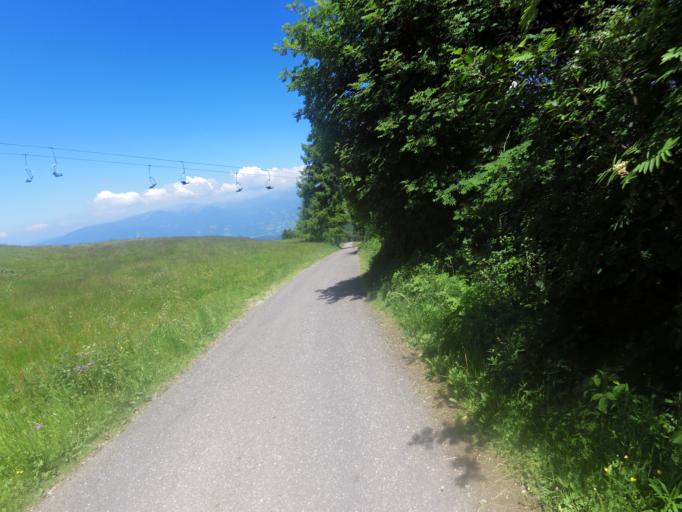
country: IT
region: Trentino-Alto Adige
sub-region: Bolzano
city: Siusi
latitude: 46.5301
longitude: 11.6020
